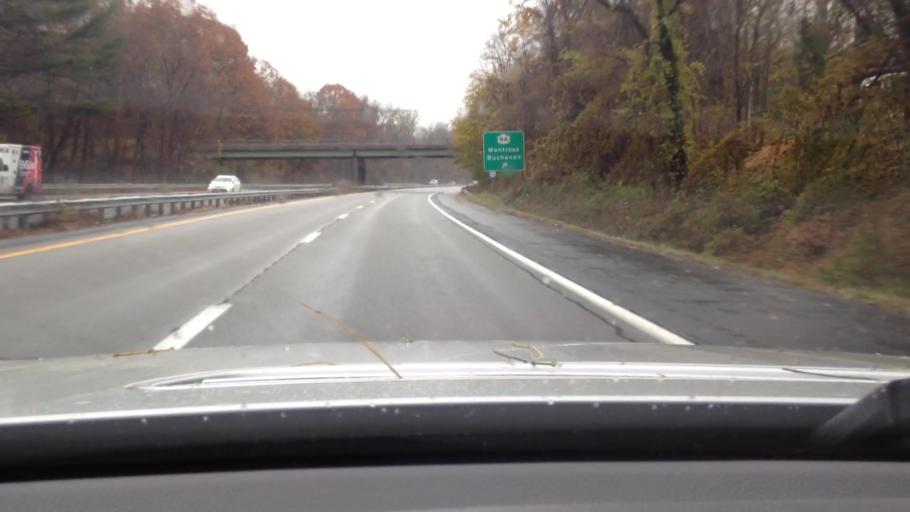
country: US
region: New York
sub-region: Westchester County
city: Crugers
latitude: 41.2374
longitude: -73.9137
